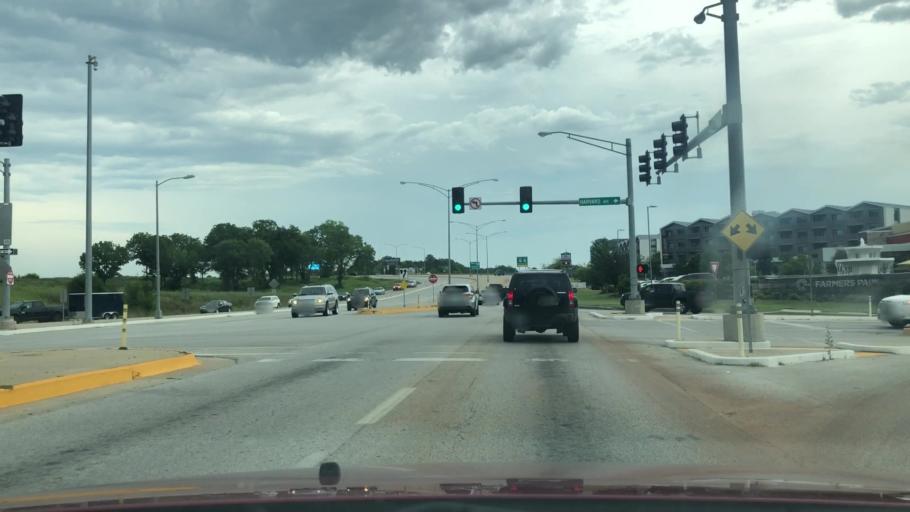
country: US
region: Missouri
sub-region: Greene County
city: Springfield
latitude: 37.1371
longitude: -93.2572
